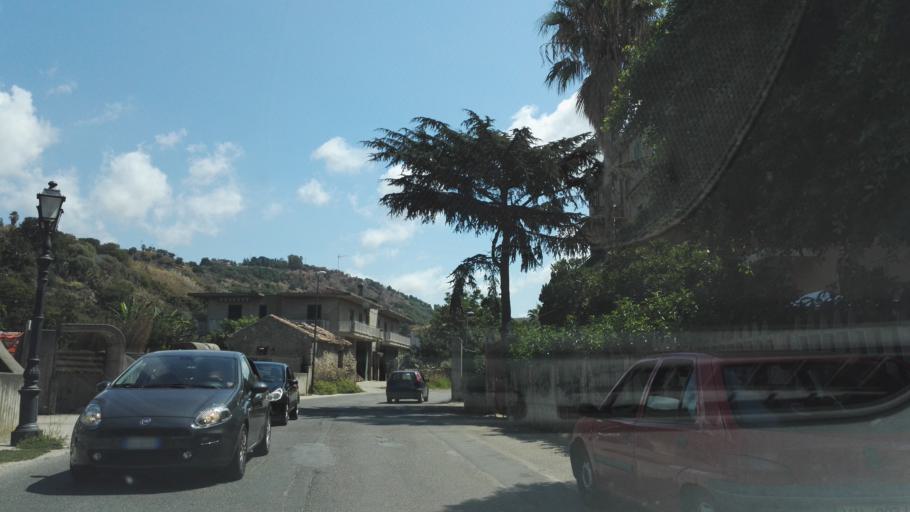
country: IT
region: Calabria
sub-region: Provincia di Vibo-Valentia
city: Nicotera
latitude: 38.5464
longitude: 15.9359
